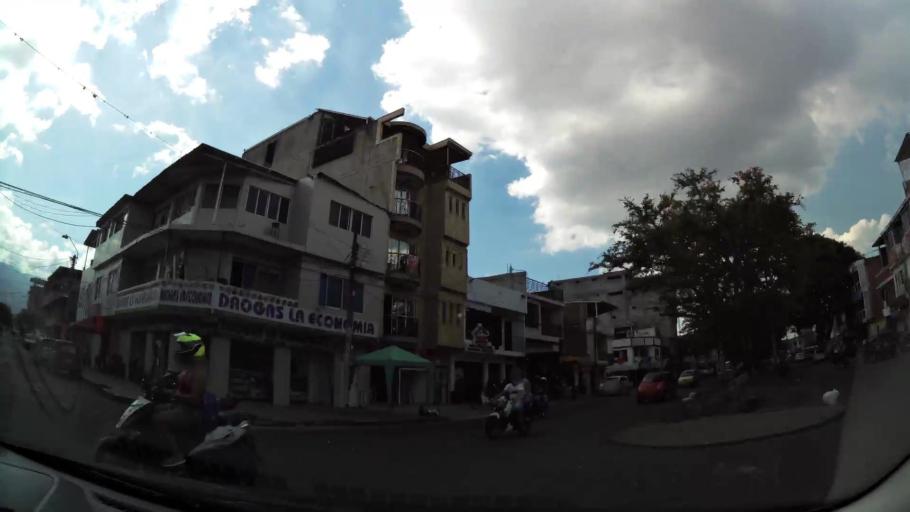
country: CO
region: Valle del Cauca
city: Cali
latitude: 3.4163
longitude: -76.5176
